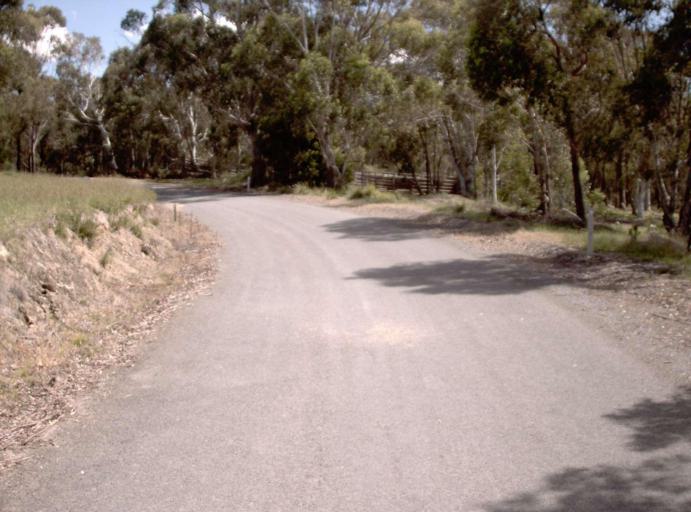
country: AU
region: New South Wales
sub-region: Bombala
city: Bombala
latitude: -37.1771
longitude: 148.6972
